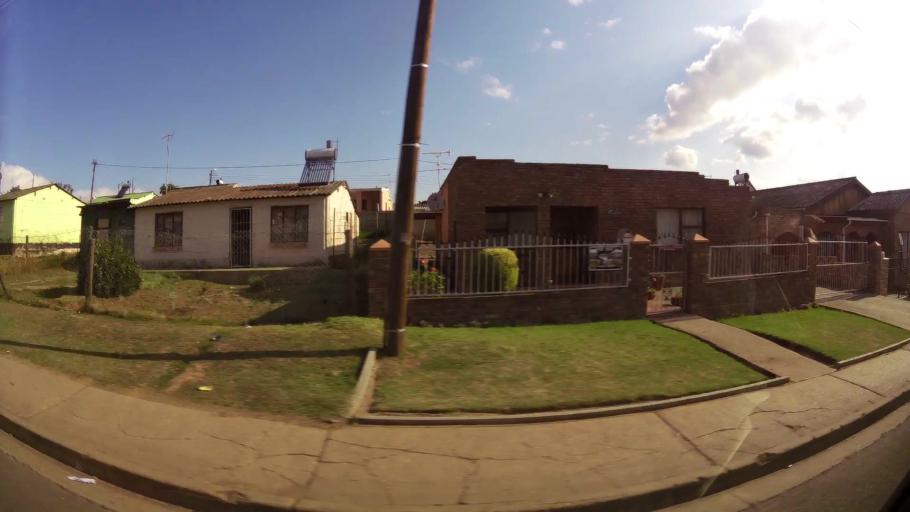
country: ZA
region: Eastern Cape
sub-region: Nelson Mandela Bay Metropolitan Municipality
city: Uitenhage
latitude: -33.7354
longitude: 25.3694
